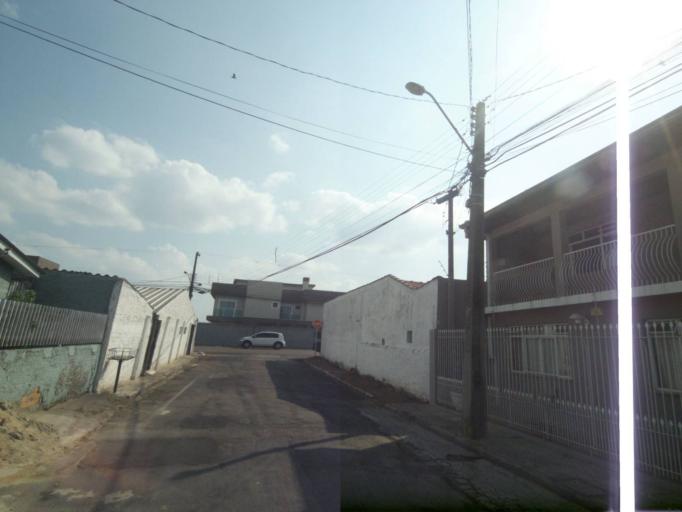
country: BR
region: Parana
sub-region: Sao Jose Dos Pinhais
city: Sao Jose dos Pinhais
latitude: -25.5053
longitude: -49.2527
